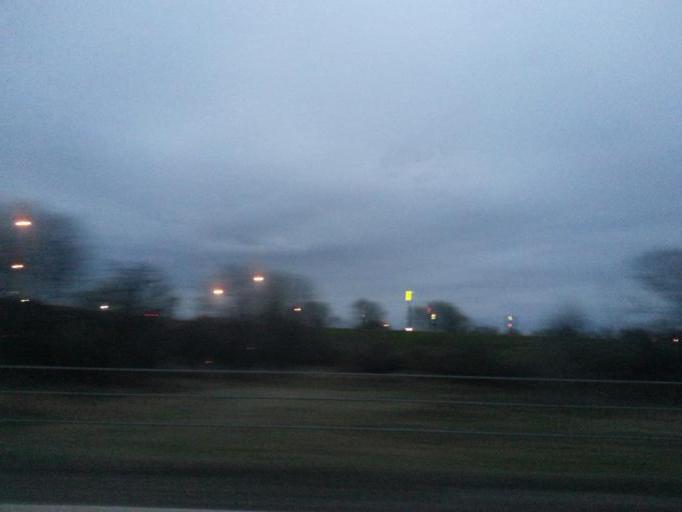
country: US
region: Iowa
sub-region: Black Hawk County
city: Elk Run Heights
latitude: 42.4574
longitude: -92.2534
